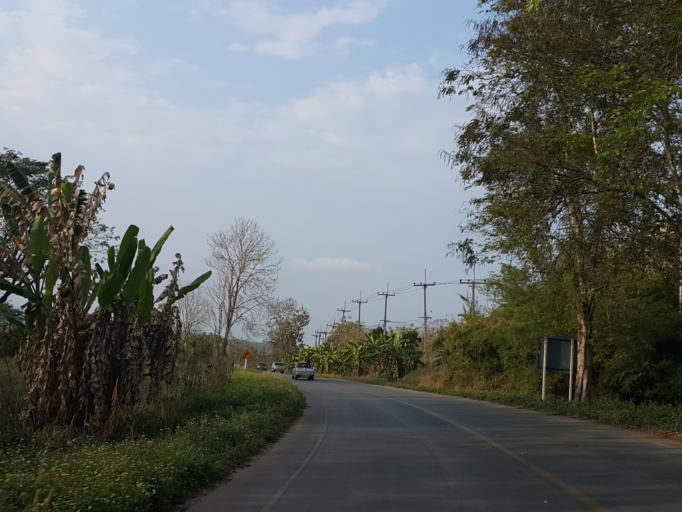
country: TH
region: Lampang
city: Hang Chat
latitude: 18.4403
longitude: 99.4506
